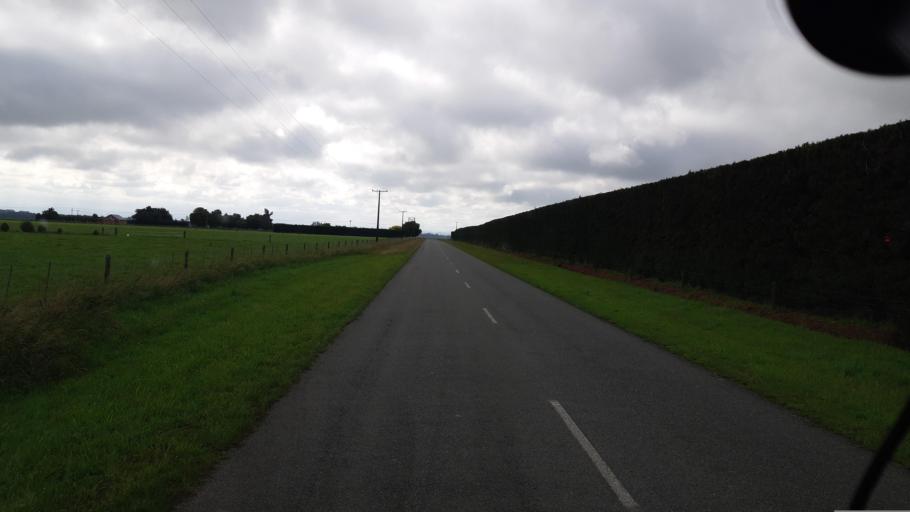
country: NZ
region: Canterbury
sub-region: Timaru District
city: Timaru
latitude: -44.2405
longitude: 171.3507
